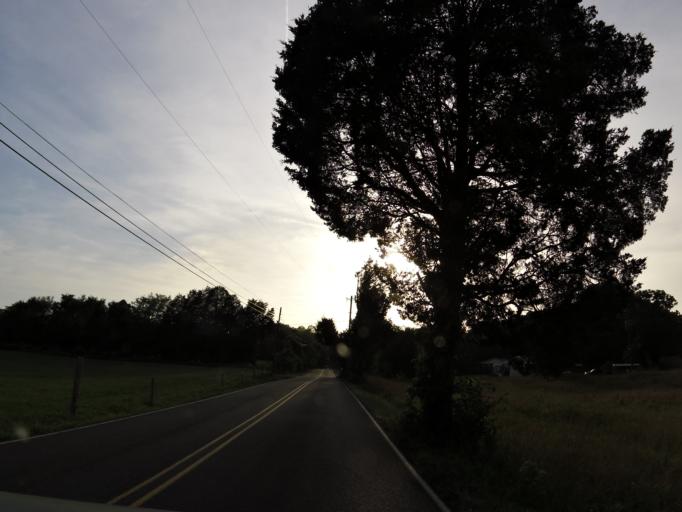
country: US
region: Tennessee
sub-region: Sevier County
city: Seymour
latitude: 35.9053
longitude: -83.8045
